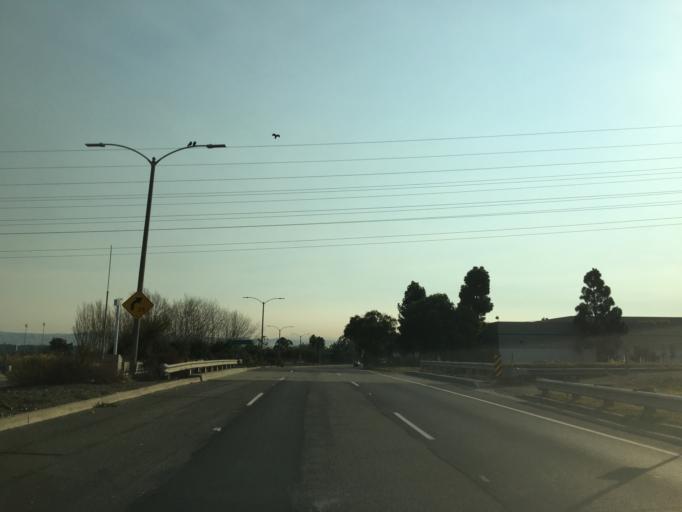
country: US
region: California
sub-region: Santa Clara County
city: Sunnyvale
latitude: 37.4148
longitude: -122.0047
